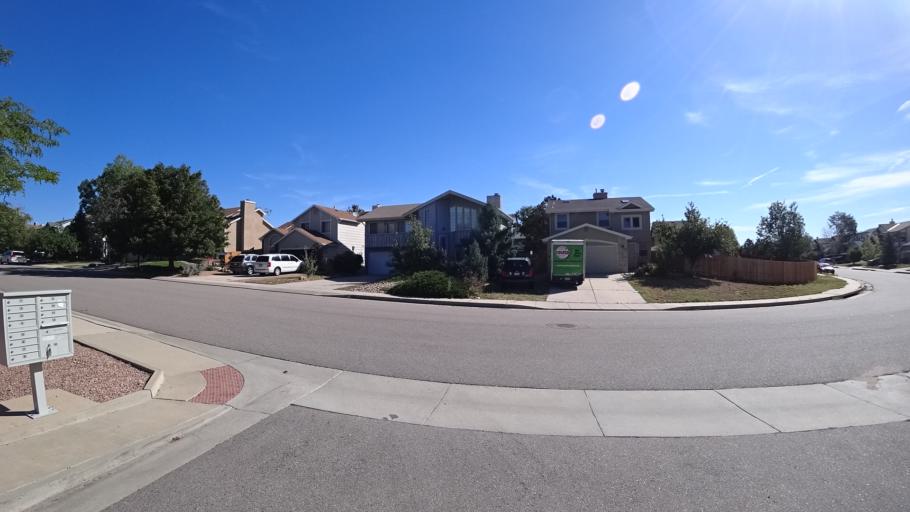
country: US
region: Colorado
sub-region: El Paso County
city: Black Forest
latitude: 38.9511
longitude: -104.7357
